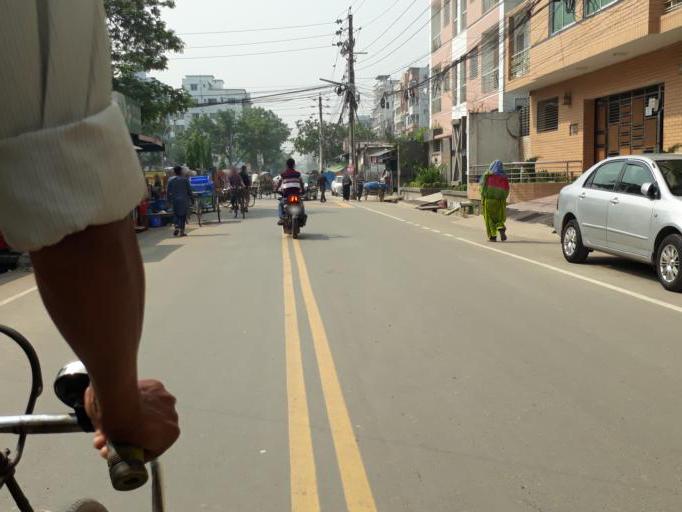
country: BD
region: Dhaka
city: Tungi
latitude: 23.8751
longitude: 90.3840
